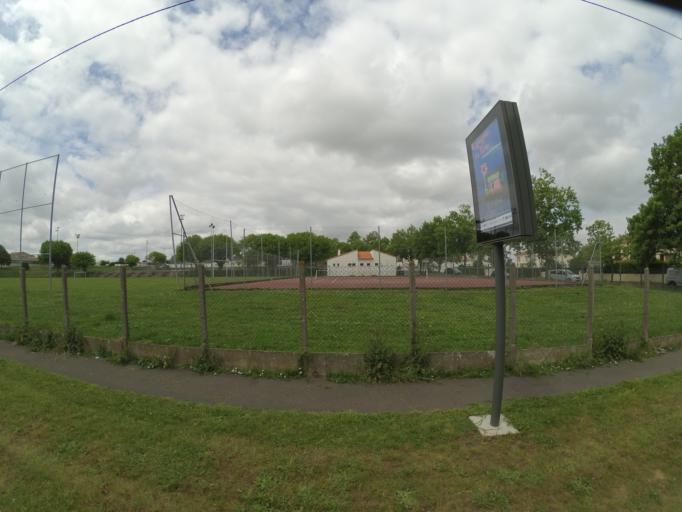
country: FR
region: Poitou-Charentes
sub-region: Departement de la Charente-Maritime
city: Rochefort
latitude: 45.9552
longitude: -0.9691
